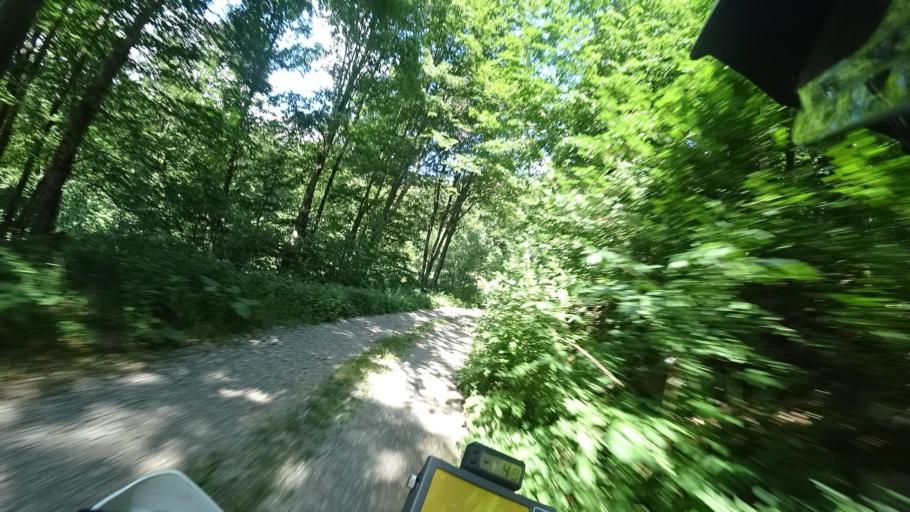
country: HR
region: Karlovacka
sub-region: Grad Ogulin
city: Ogulin
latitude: 45.1671
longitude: 15.1186
